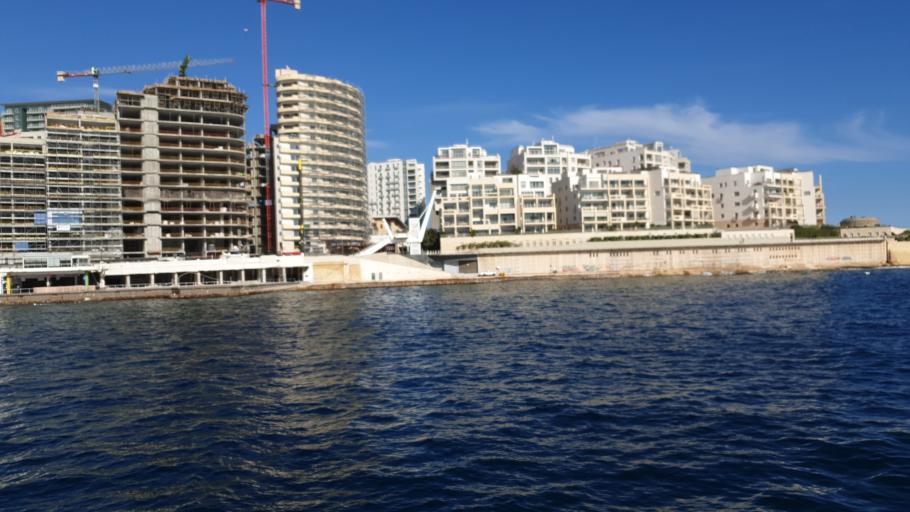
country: MT
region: Il-Belt Valletta
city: Valletta
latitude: 35.9050
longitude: 14.5088
